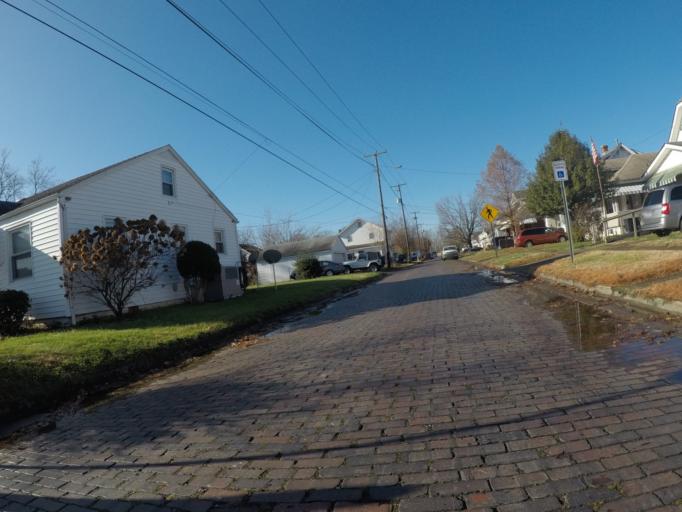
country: US
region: Ohio
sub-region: Lawrence County
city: Burlington
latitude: 38.4083
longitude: -82.4976
